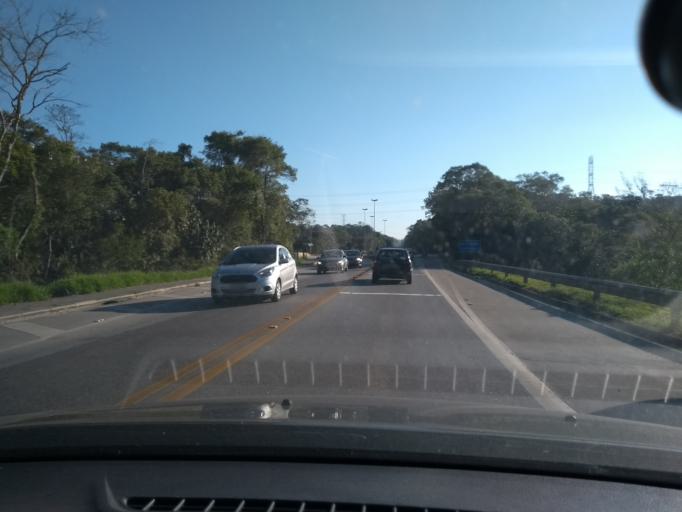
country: BR
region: Sao Paulo
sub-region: Rio Grande Da Serra
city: Rio Grande da Serra
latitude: -23.7663
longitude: -46.4670
